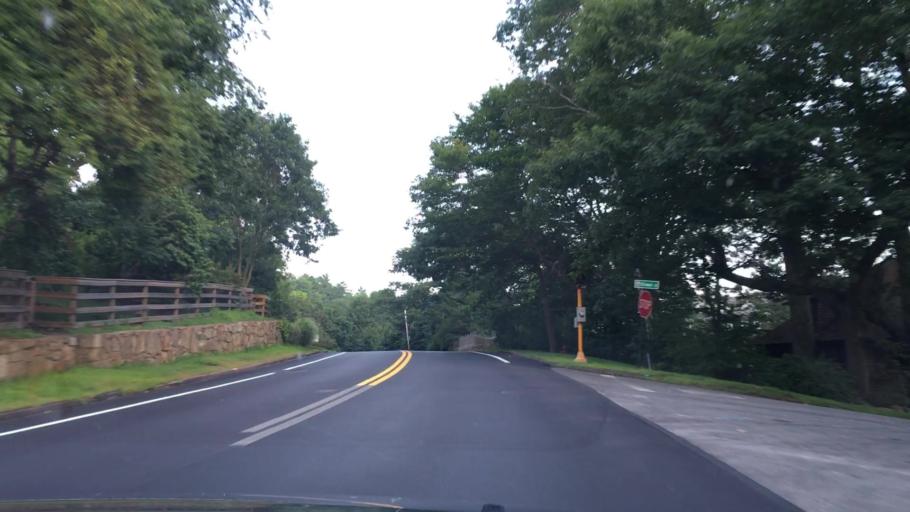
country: US
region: Massachusetts
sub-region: Essex County
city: Essex
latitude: 42.5802
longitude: -70.7313
